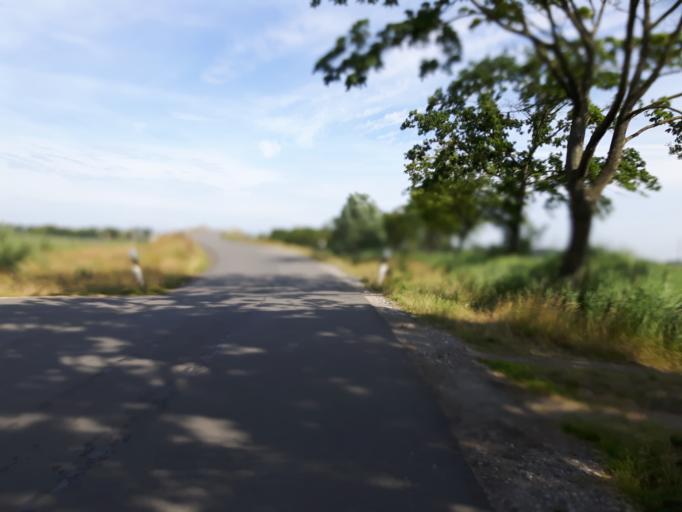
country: DE
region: Lower Saxony
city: Elsfleth
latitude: 53.1926
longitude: 8.4871
